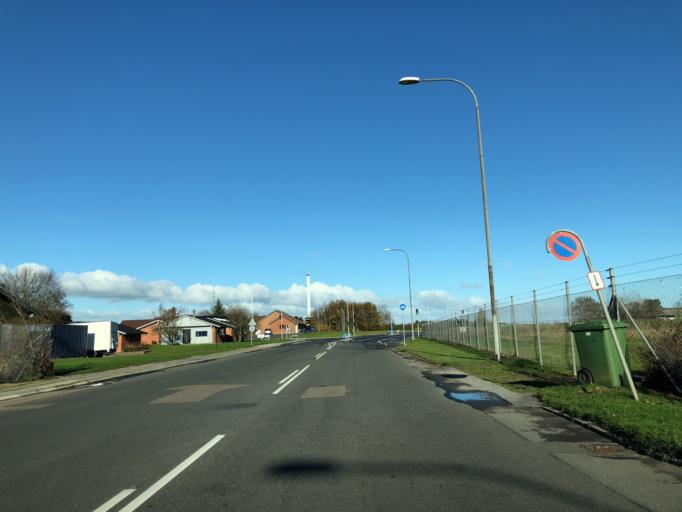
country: DK
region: Central Jutland
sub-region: Holstebro Kommune
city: Holstebro
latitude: 56.3843
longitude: 8.6209
